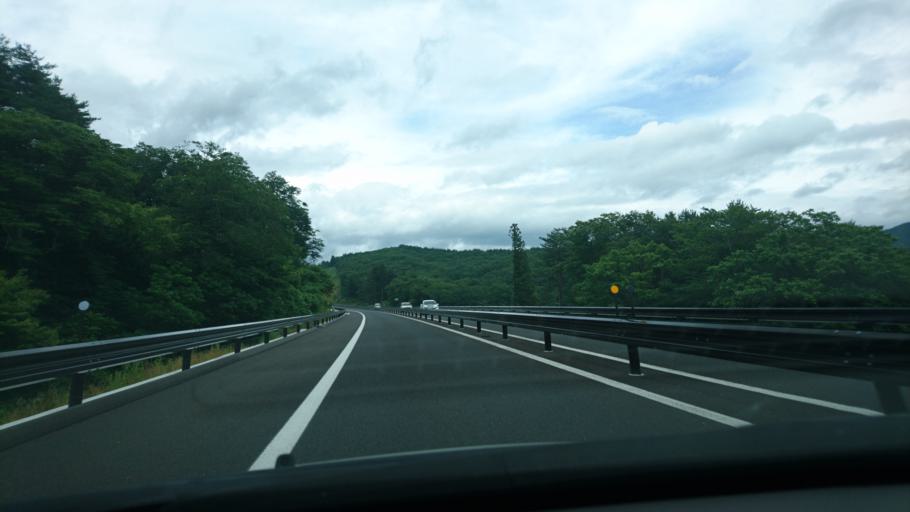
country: JP
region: Iwate
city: Yamada
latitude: 39.5448
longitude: 141.9237
